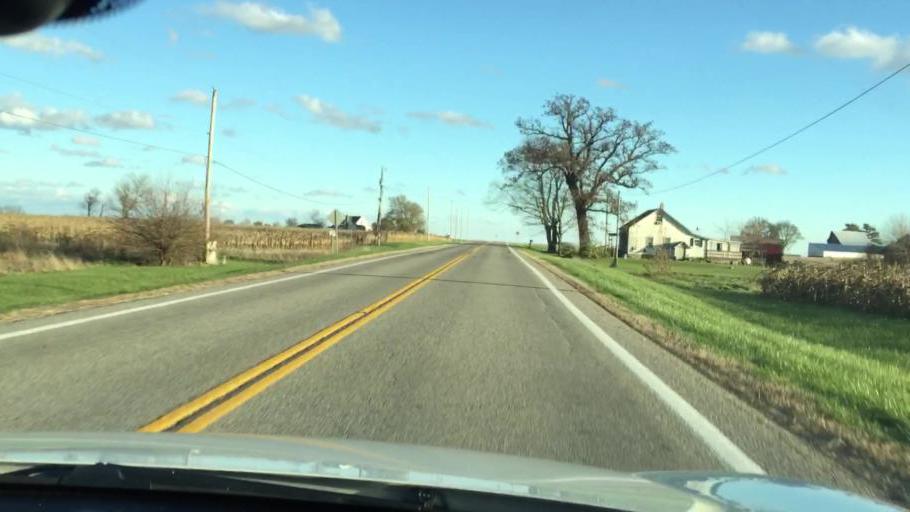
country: US
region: Ohio
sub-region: Champaign County
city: North Lewisburg
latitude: 40.1906
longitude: -83.5221
